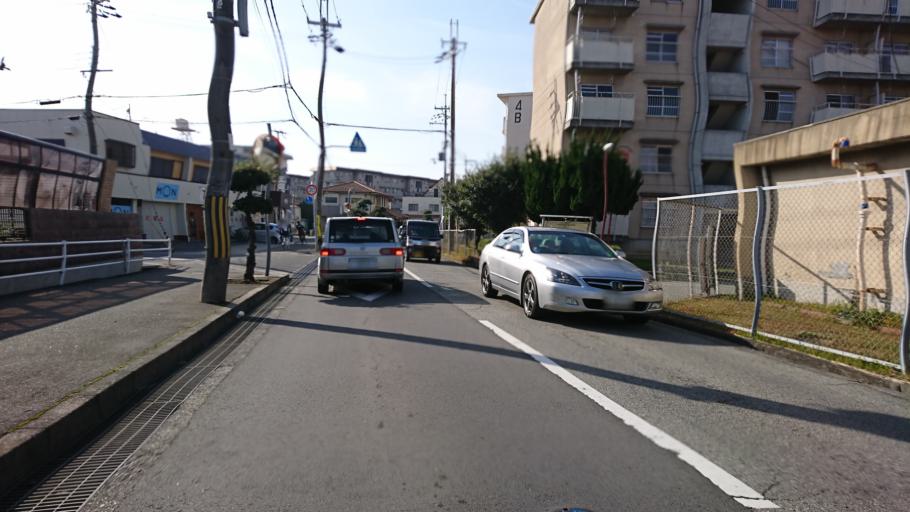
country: JP
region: Hyogo
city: Kakogawacho-honmachi
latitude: 34.7300
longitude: 134.8792
